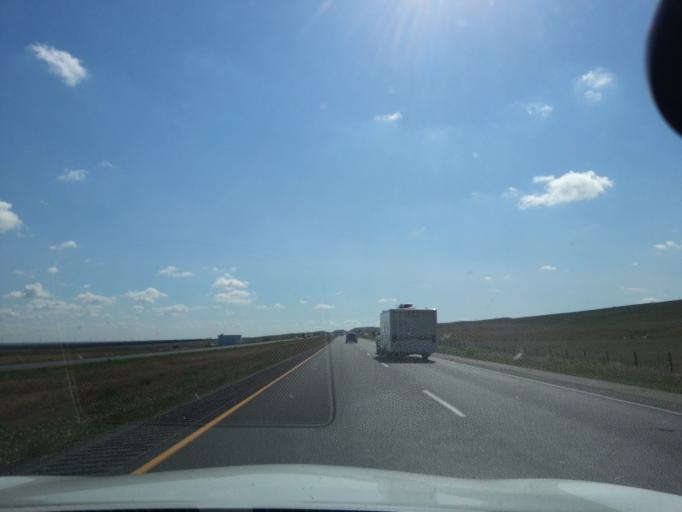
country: US
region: California
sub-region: Fresno County
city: Coalinga
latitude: 36.3441
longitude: -120.3124
